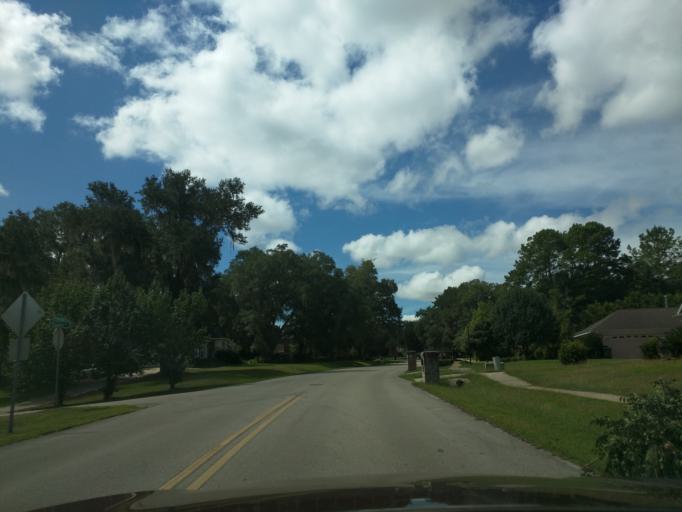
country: US
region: Florida
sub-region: Leon County
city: Tallahassee
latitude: 30.5748
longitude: -84.2523
